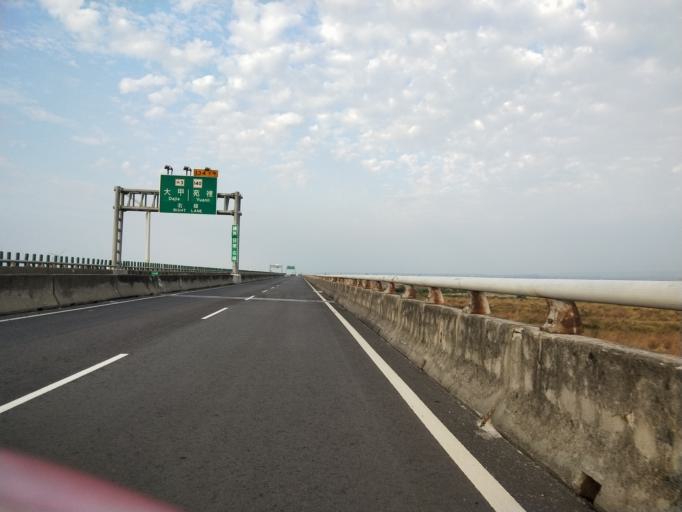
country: TW
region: Taiwan
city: Fengyuan
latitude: 24.3993
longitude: 120.6091
